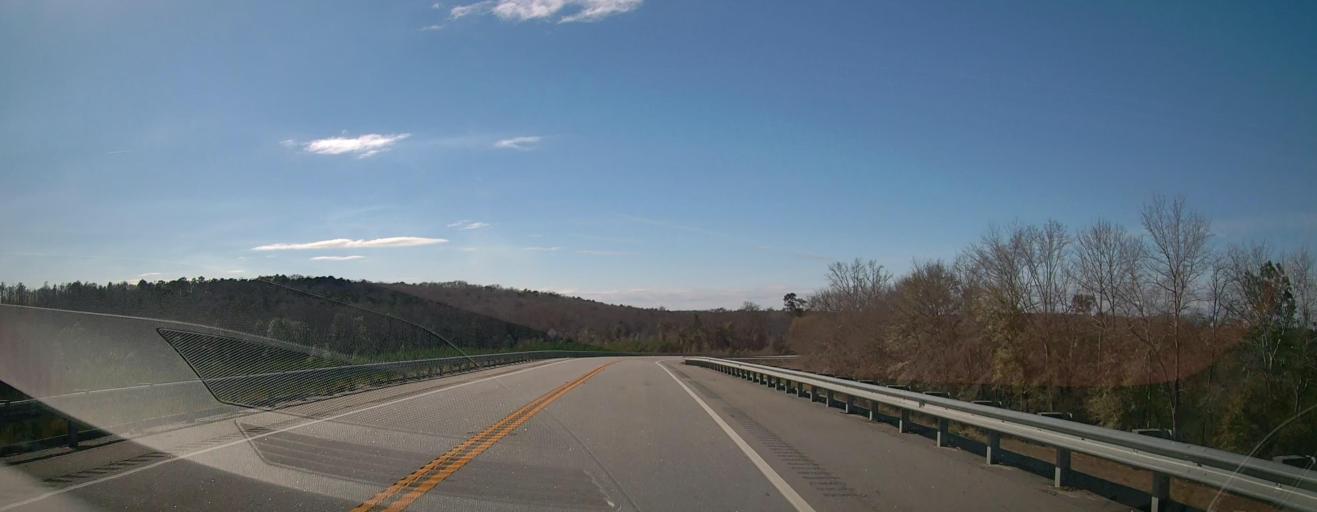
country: US
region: Georgia
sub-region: Macon County
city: Oglethorpe
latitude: 32.3457
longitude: -84.1415
